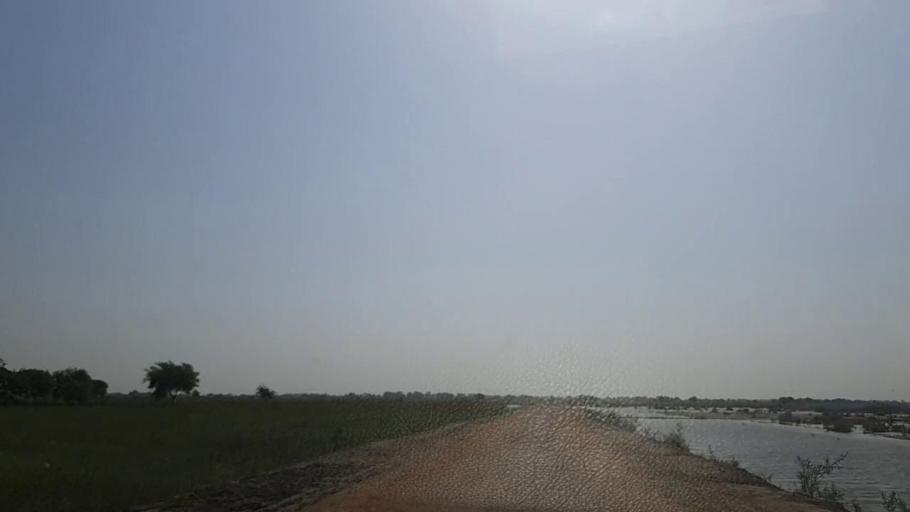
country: PK
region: Sindh
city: Daro Mehar
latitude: 24.7060
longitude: 68.1265
